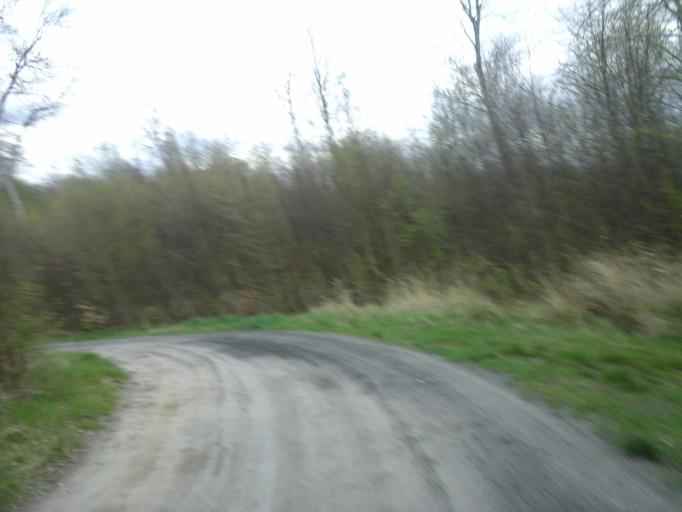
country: PL
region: West Pomeranian Voivodeship
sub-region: Powiat choszczenski
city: Bierzwnik
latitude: 53.0660
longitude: 15.5868
